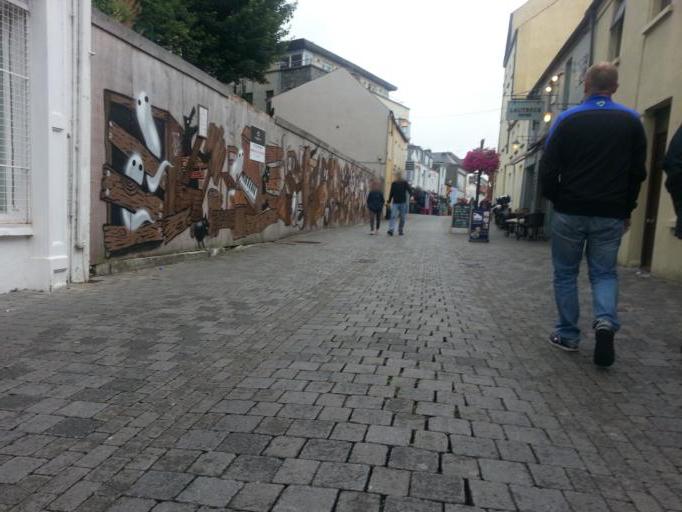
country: IE
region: Leinster
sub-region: Kilkenny
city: Kilkenny
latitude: 52.6520
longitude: -7.2517
